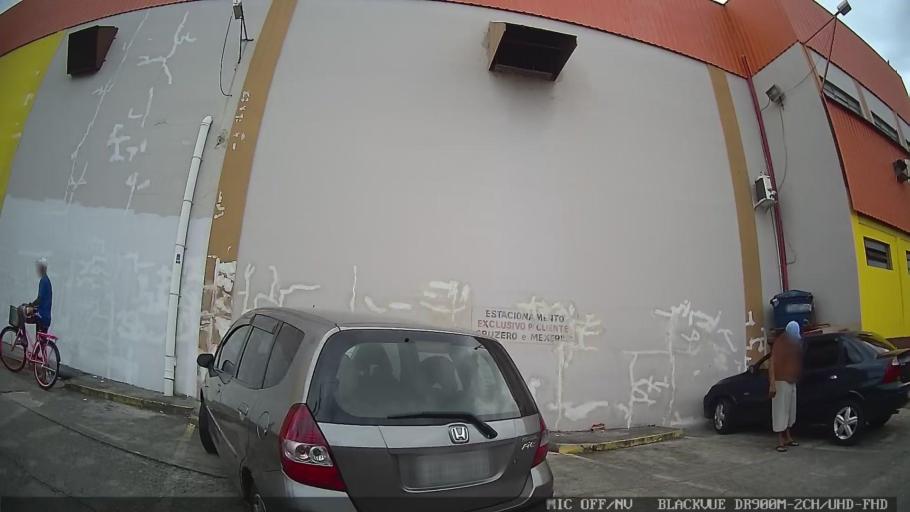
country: BR
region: Sao Paulo
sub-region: Caraguatatuba
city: Caraguatatuba
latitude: -23.6790
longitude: -45.4490
